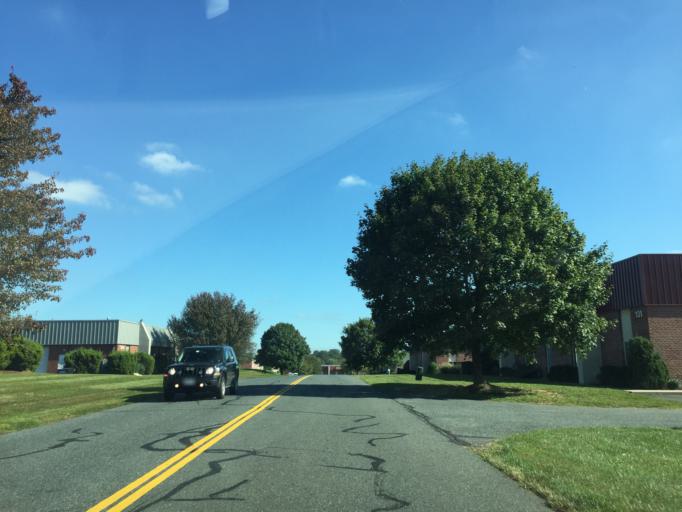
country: US
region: Maryland
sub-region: Harford County
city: Bel Air North
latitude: 39.5773
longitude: -76.3722
